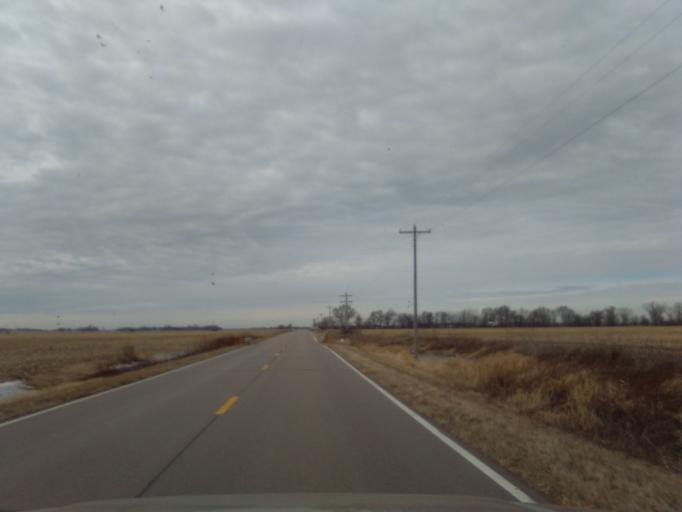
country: US
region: Nebraska
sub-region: Hall County
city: Grand Island
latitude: 40.7711
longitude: -98.4293
